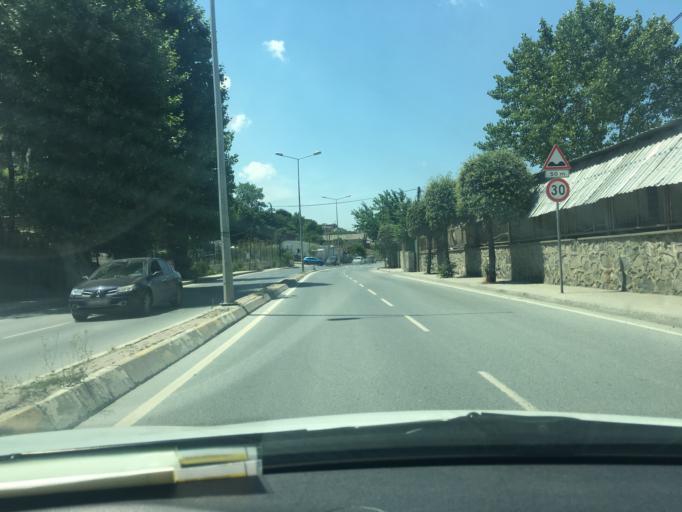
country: TR
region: Istanbul
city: Sisli
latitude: 41.0874
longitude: 28.9361
